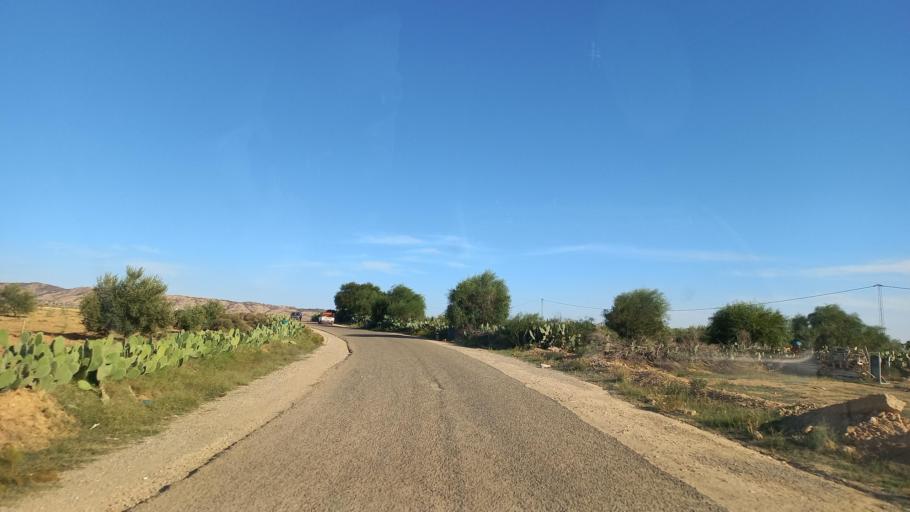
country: TN
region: Al Qasrayn
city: Sbiba
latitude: 35.3347
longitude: 9.0894
